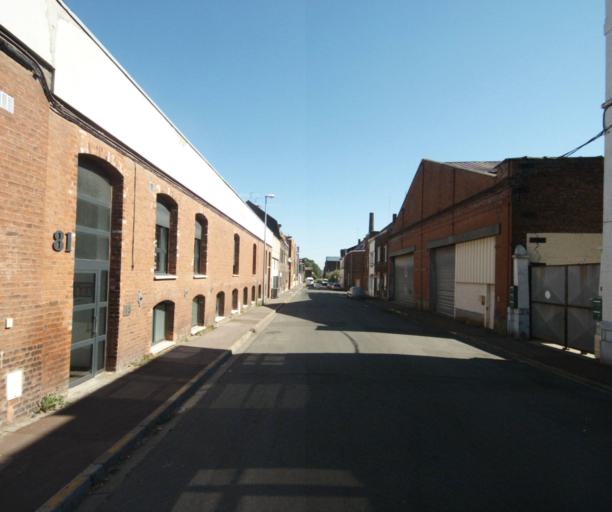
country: FR
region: Nord-Pas-de-Calais
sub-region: Departement du Nord
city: Tourcoing
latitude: 50.7203
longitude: 3.1742
